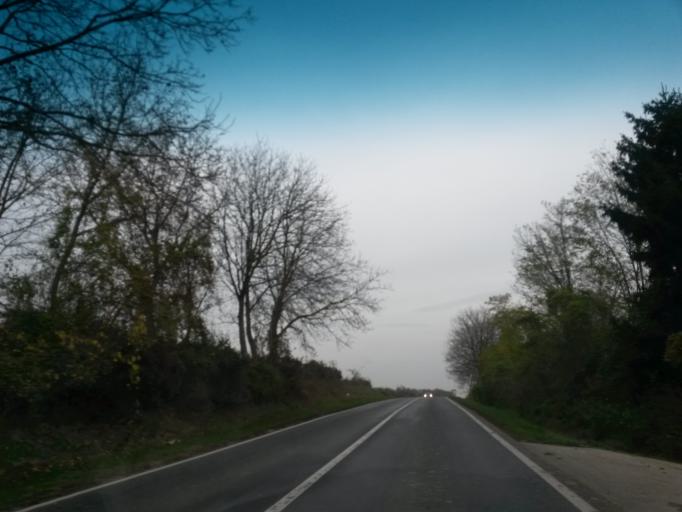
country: HR
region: Vukovarsko-Srijemska
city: Slakovci
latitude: 45.2133
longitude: 18.9903
